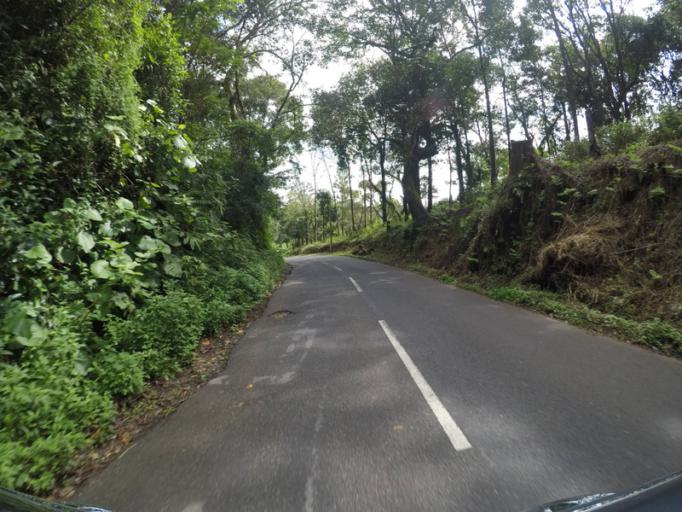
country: IN
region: Karnataka
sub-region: Kodagu
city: Madikeri
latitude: 12.4543
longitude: 75.7627
